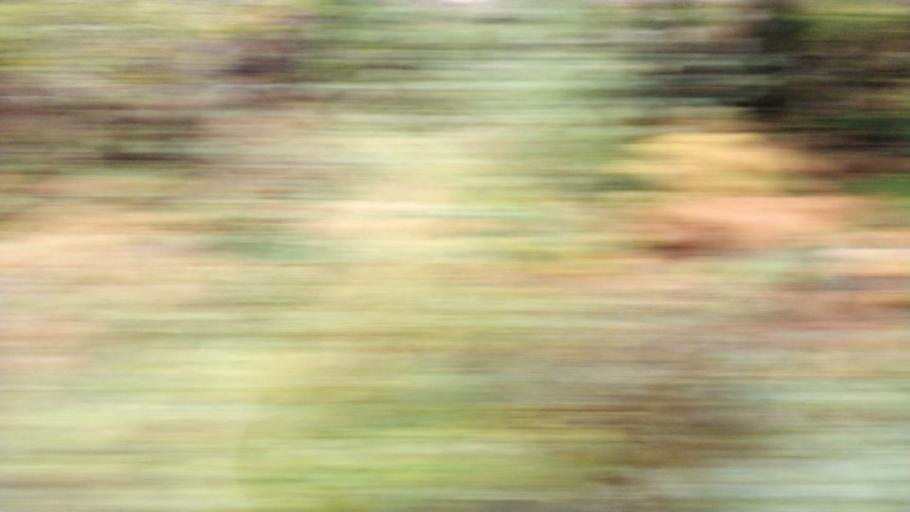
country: GB
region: England
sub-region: Borough of Bolton
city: Westhoughton
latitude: 53.5401
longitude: -2.5188
